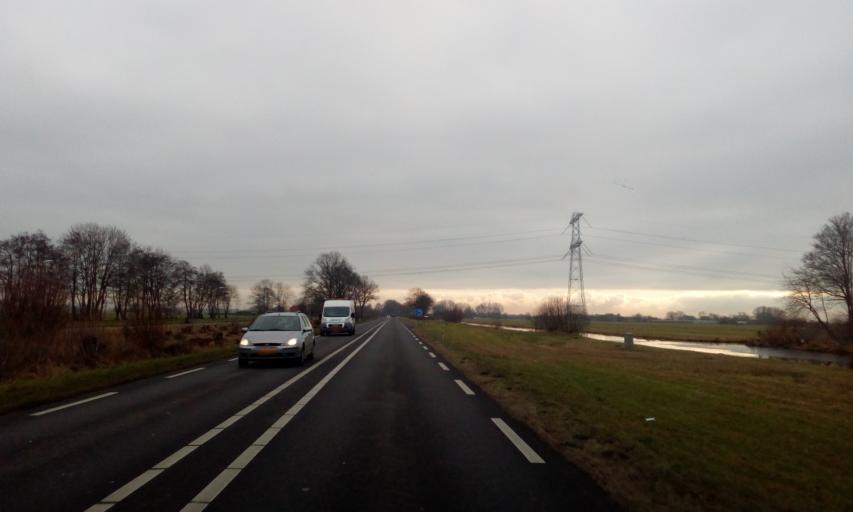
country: NL
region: South Holland
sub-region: Gemeente Gouda
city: Gouda
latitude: 51.9966
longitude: 4.7382
